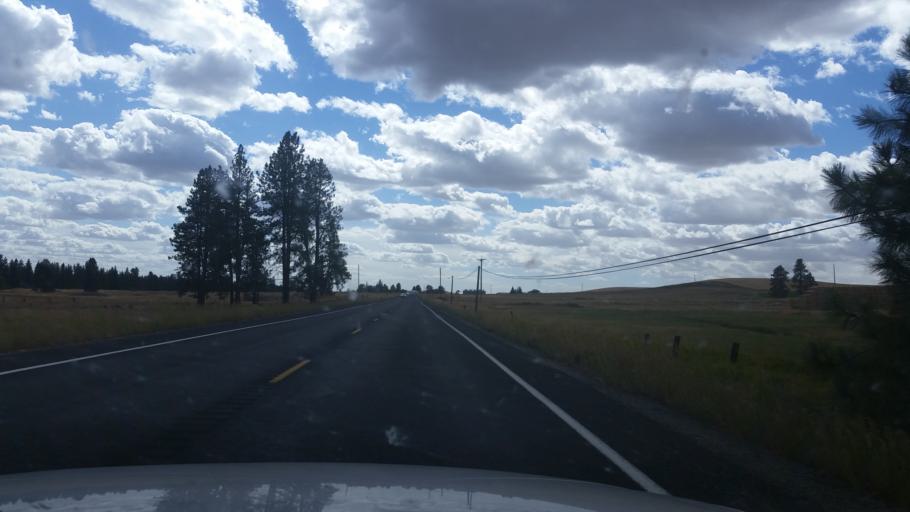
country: US
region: Washington
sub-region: Spokane County
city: Medical Lake
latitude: 47.5382
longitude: -117.7093
